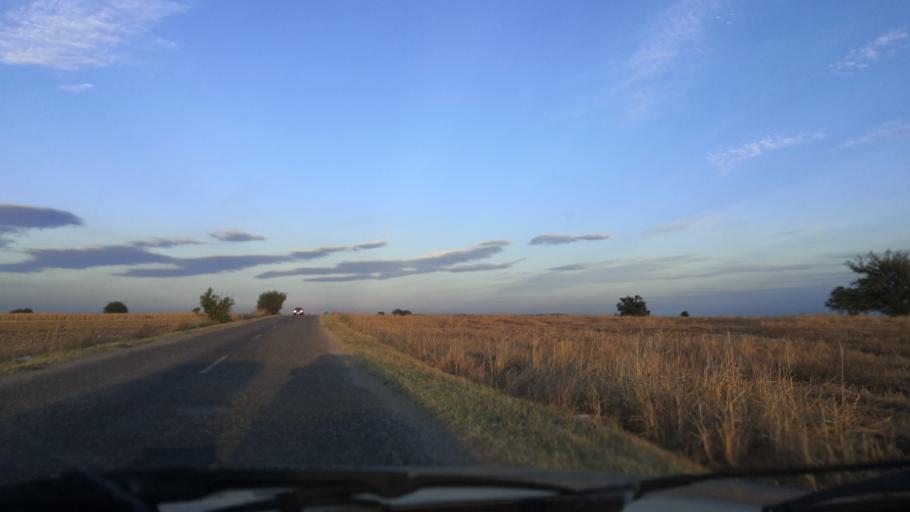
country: RO
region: Mehedinti
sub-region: Comuna Gruia
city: Izvoarele
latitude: 44.2538
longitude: 22.6244
